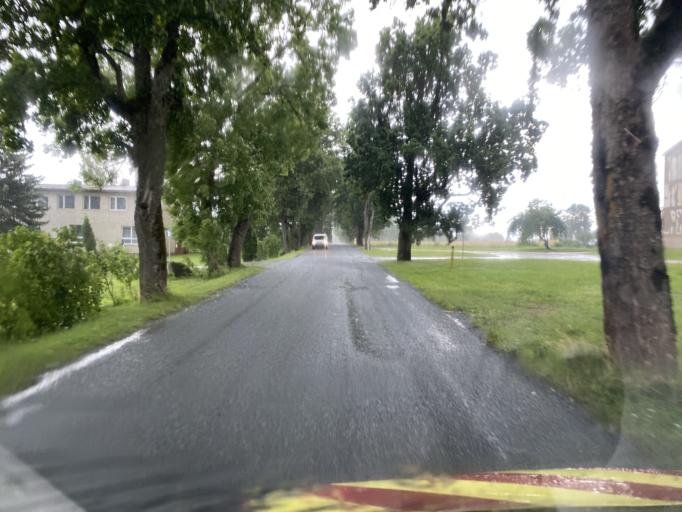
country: EE
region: Valgamaa
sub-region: Torva linn
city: Torva
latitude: 58.1406
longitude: 25.8048
